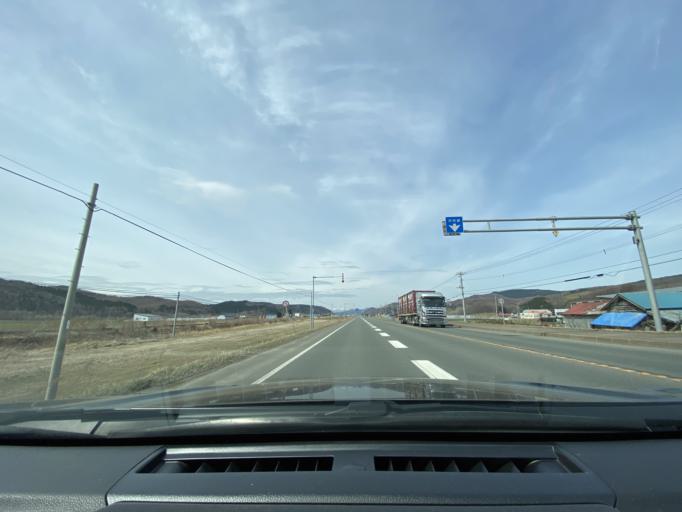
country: JP
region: Hokkaido
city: Kitami
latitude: 43.7918
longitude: 143.7080
